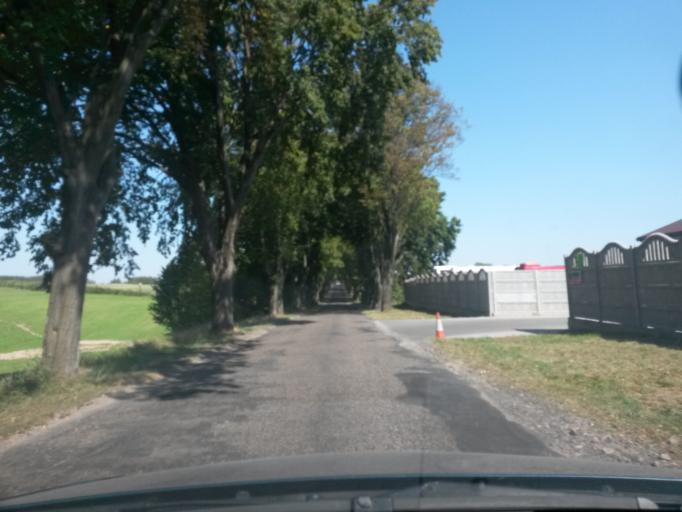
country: PL
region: Kujawsko-Pomorskie
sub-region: Powiat brodnicki
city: Gorzno
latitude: 53.2091
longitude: 19.6358
